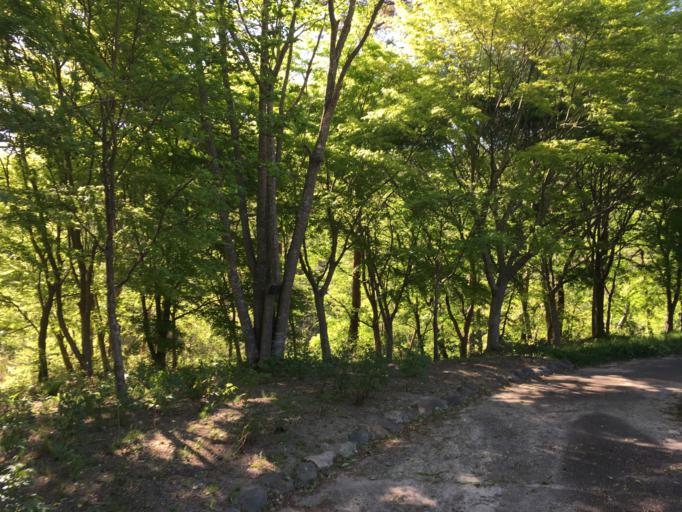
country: JP
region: Iwate
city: Ichinoseki
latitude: 38.8265
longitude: 141.2216
